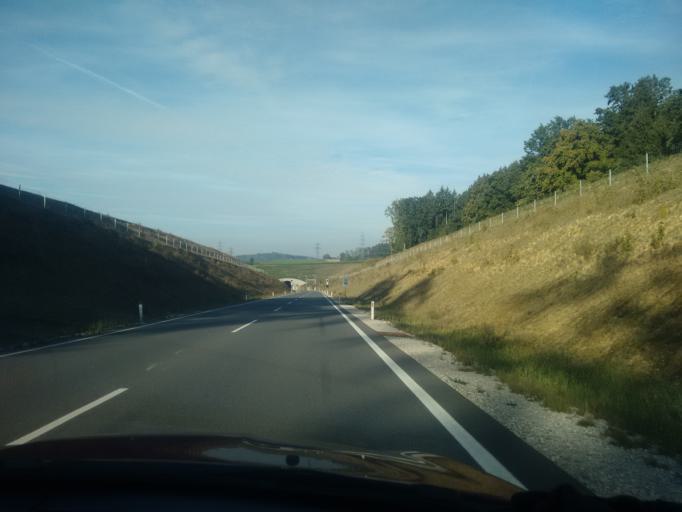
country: AT
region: Upper Austria
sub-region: Wels-Land
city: Lambach
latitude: 48.1014
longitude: 13.8747
